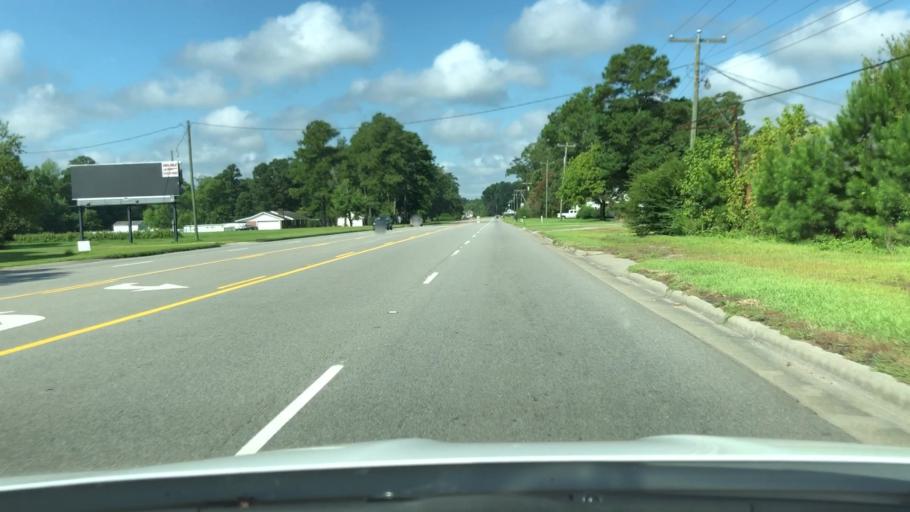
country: US
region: North Carolina
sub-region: Bertie County
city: Windsor
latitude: 36.0341
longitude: -76.7865
